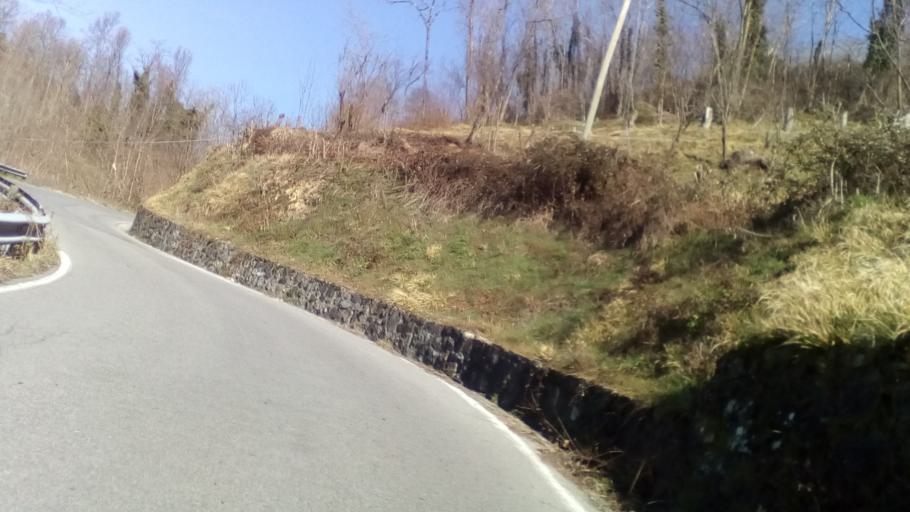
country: IT
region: Tuscany
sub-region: Provincia di Lucca
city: Castiglione di Garfagnana
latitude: 44.1407
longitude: 10.4268
